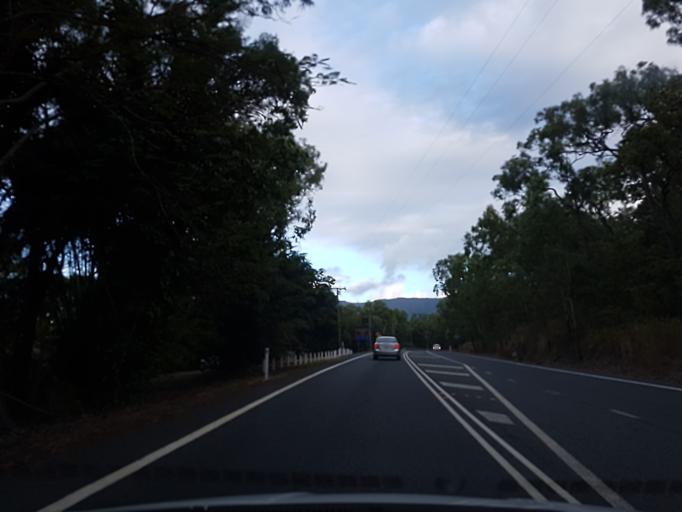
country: AU
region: Queensland
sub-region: Cairns
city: Palm Cove
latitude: -16.6574
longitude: 145.5658
